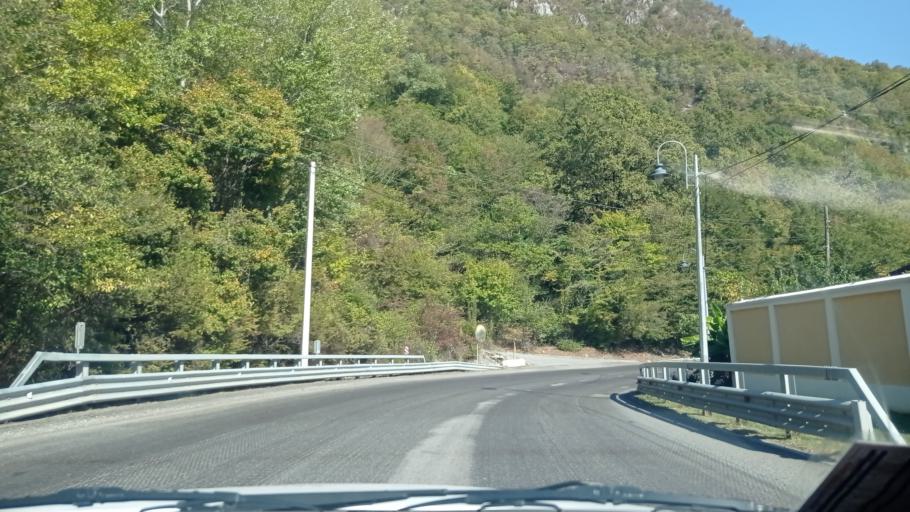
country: RU
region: Krasnodarskiy
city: Vysokoye
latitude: 43.5926
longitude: 40.0082
